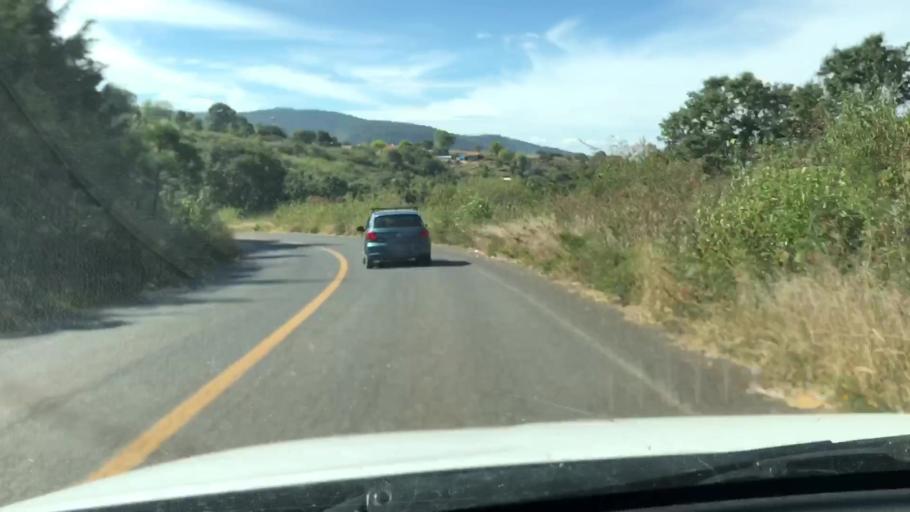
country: MX
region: Jalisco
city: Chiquilistlan
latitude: 20.1412
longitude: -103.7181
